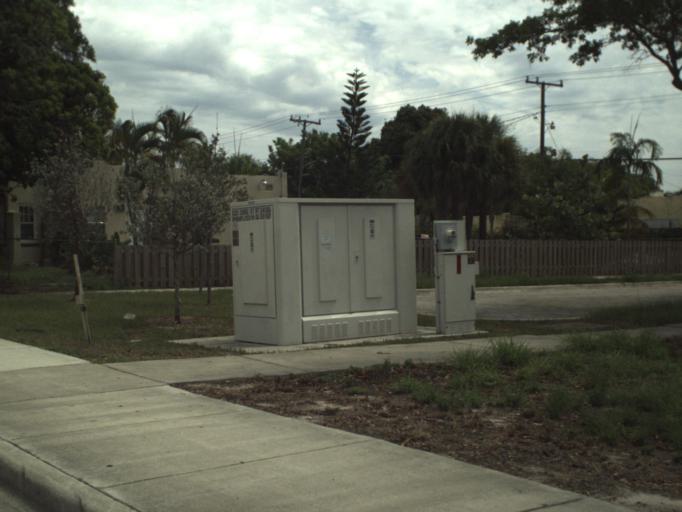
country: US
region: Florida
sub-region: Palm Beach County
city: Mangonia Park
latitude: 26.7432
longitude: -80.0565
